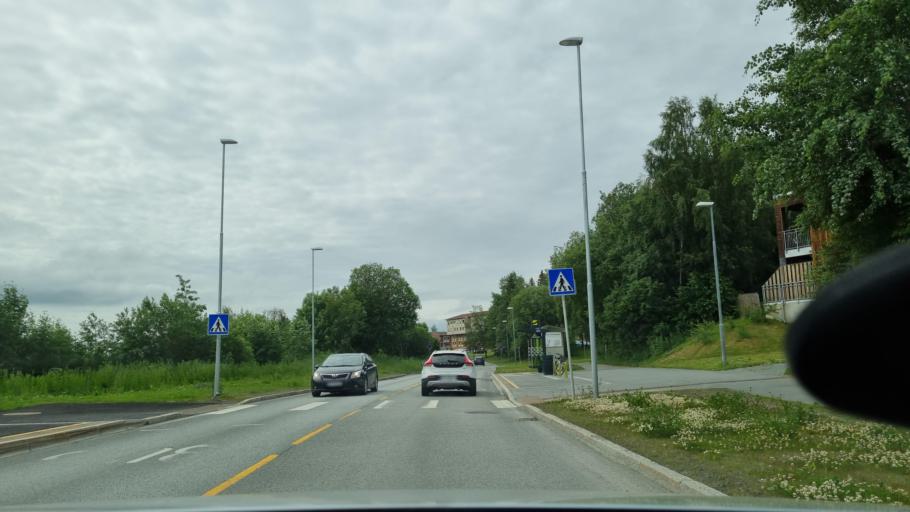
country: NO
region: Sor-Trondelag
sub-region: Melhus
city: Melhus
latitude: 63.3472
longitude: 10.3465
